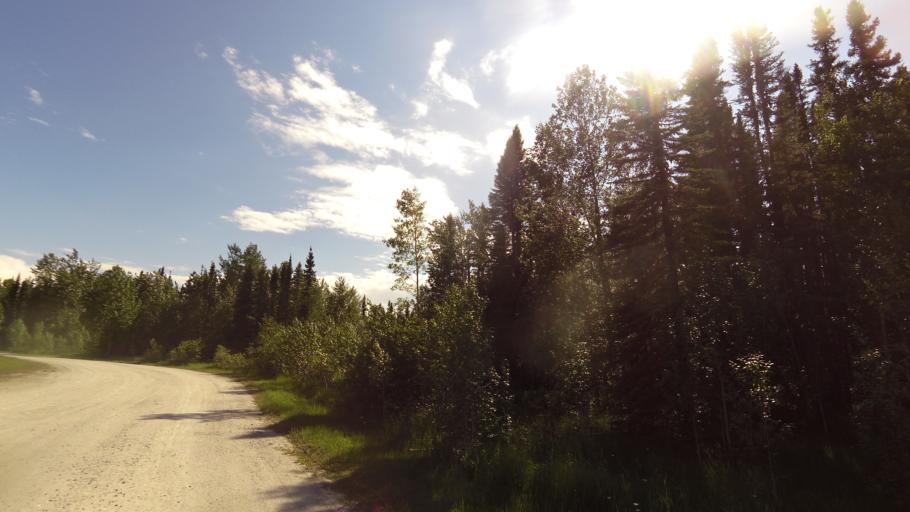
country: CA
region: Ontario
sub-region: Algoma
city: Hornepayne
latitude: 49.7681
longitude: -84.7723
